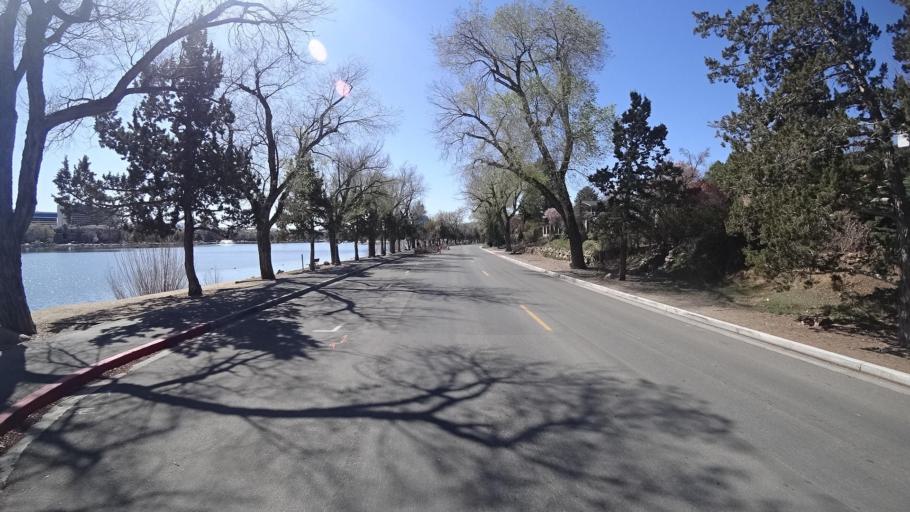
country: US
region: Nevada
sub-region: Washoe County
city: Reno
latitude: 39.5020
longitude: -119.8077
